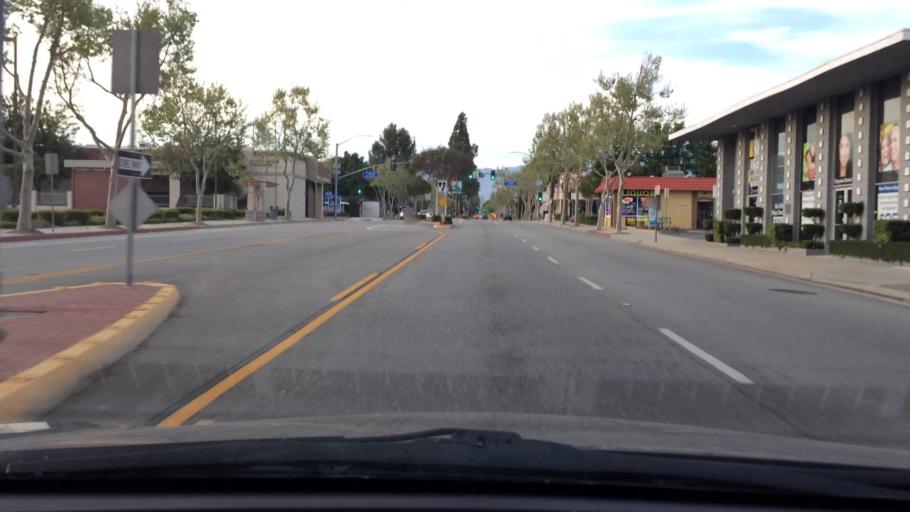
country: US
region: California
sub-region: San Bernardino County
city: Chino
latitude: 34.0145
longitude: -117.6893
